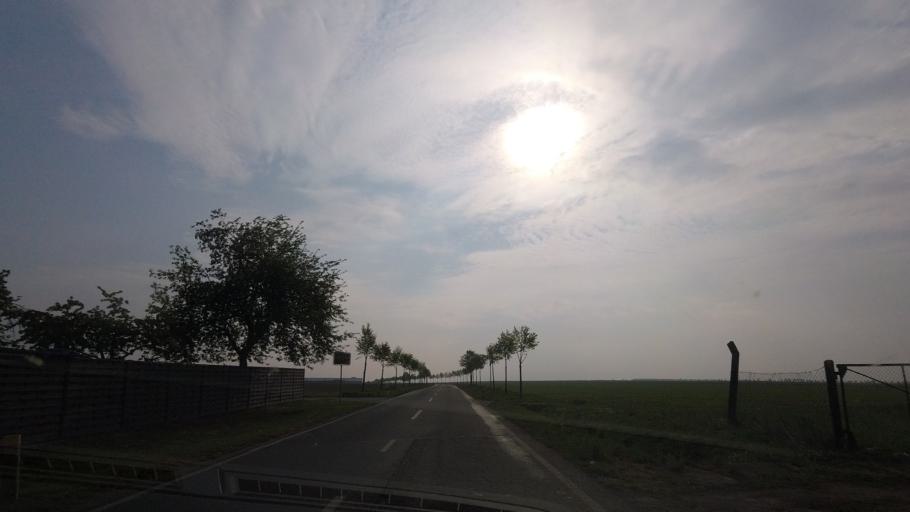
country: DE
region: Brandenburg
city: Juterbog
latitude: 51.9292
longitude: 13.1421
